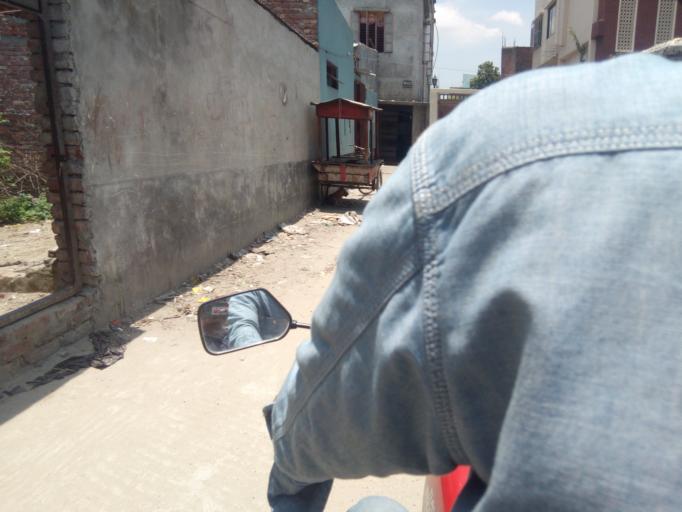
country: BD
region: Dhaka
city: Paltan
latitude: 23.7566
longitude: 90.4339
